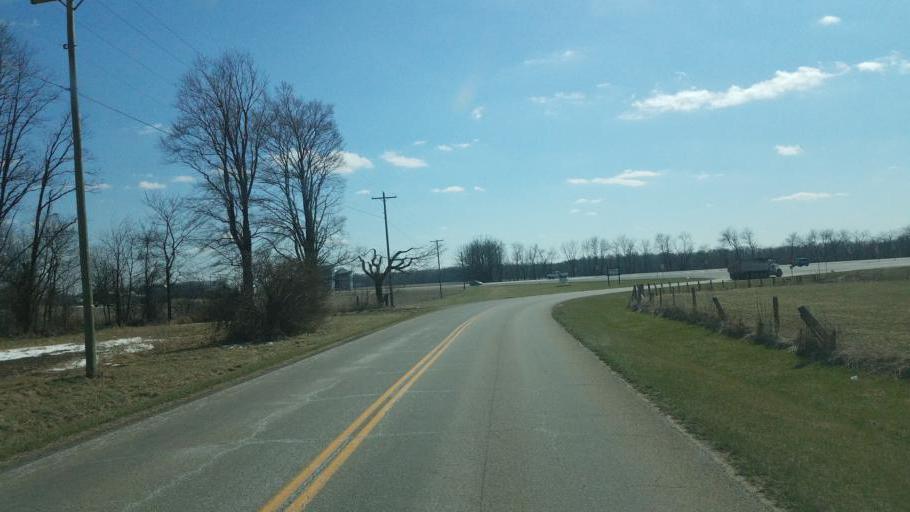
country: US
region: Ohio
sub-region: Knox County
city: Fredericktown
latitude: 40.4549
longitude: -82.5419
